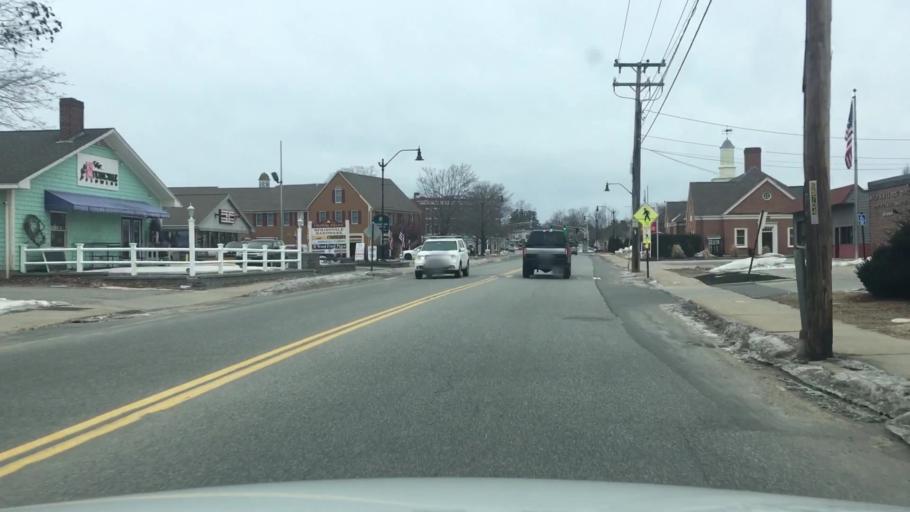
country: US
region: Maine
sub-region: York County
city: Springvale
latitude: 43.4637
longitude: -70.7959
